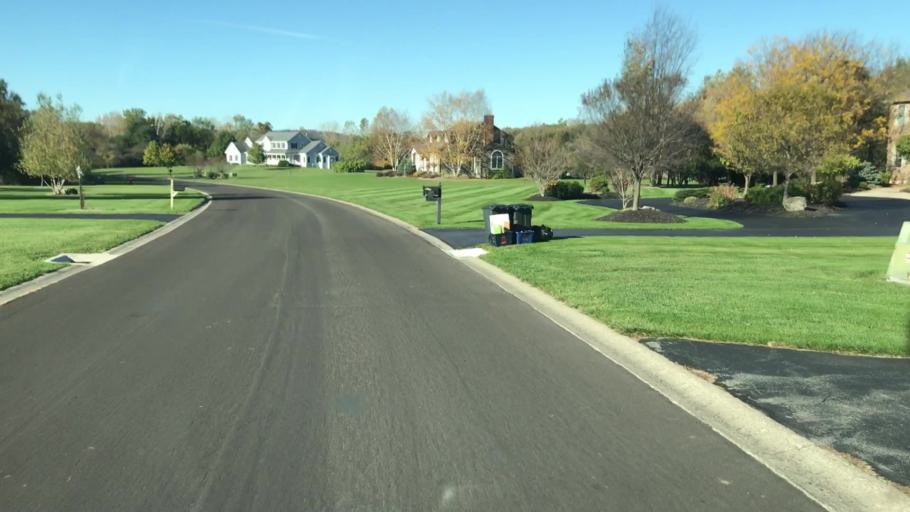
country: US
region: New York
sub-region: Onondaga County
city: Fayetteville
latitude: 42.9884
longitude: -76.0459
